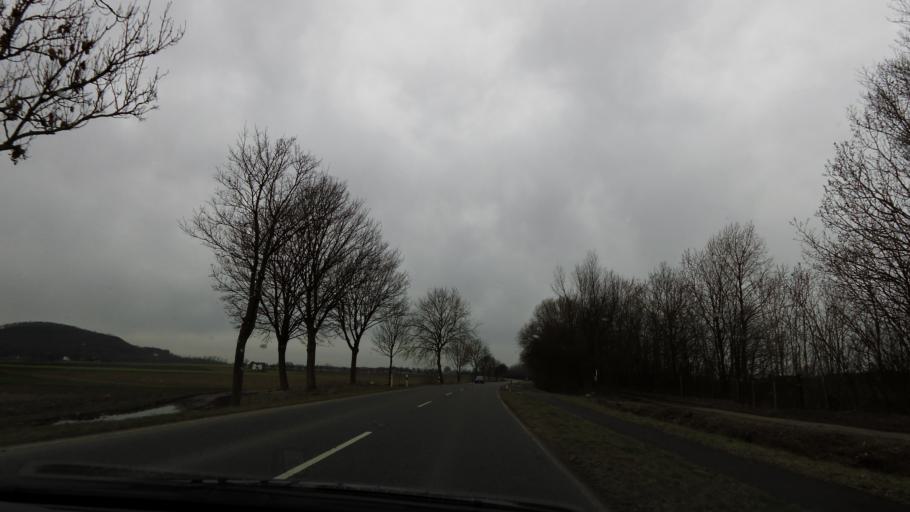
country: DE
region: North Rhine-Westphalia
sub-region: Regierungsbezirk Koln
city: Ubach-Palenberg
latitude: 50.9091
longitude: 6.1014
